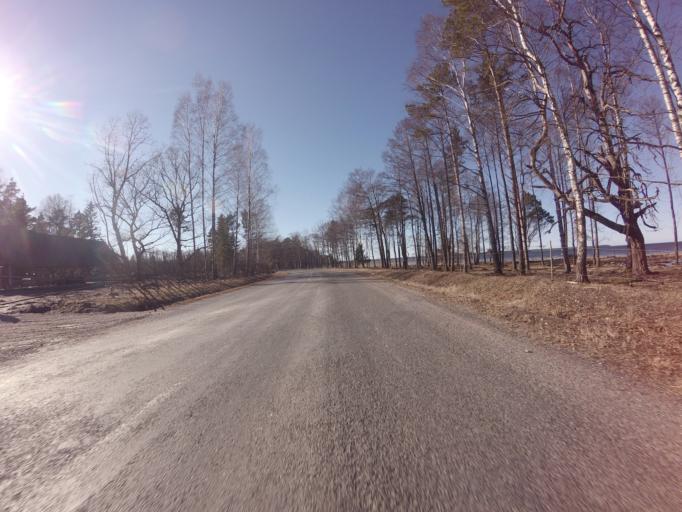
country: EE
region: Saare
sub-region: Kuressaare linn
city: Kuressaare
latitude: 58.4857
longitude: 22.2763
